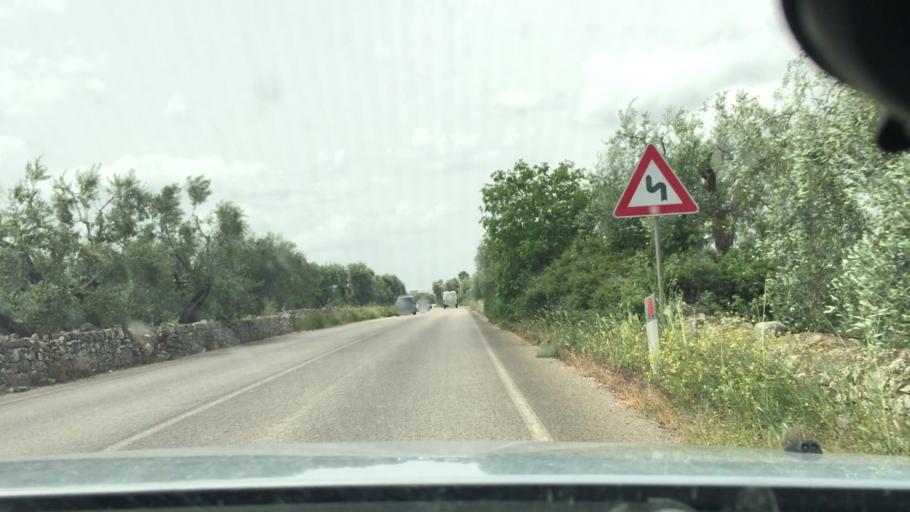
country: IT
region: Apulia
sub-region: Provincia di Bari
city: Capurso
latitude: 41.0422
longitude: 16.9432
